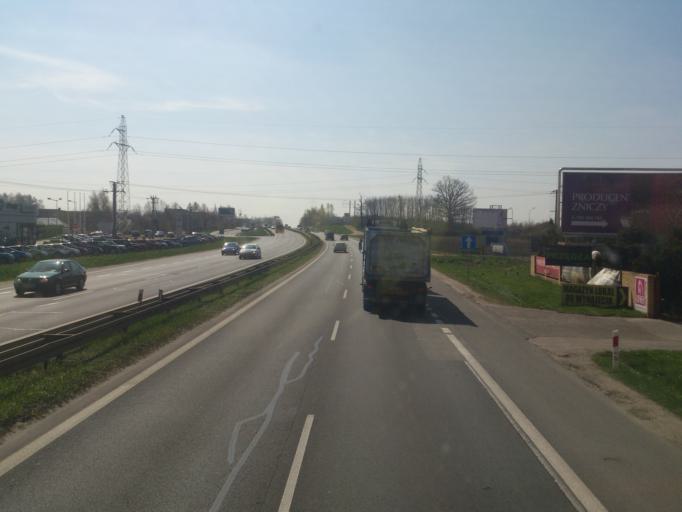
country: PL
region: Lodz Voivodeship
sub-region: Powiat lodzki wschodni
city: Starowa Gora
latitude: 51.6876
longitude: 19.4764
